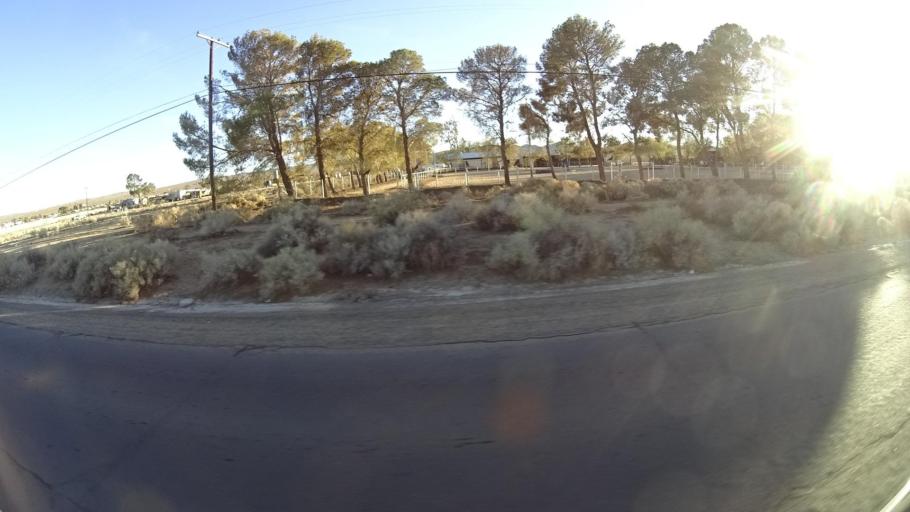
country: US
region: California
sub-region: Kern County
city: Ridgecrest
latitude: 35.6080
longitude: -117.6418
